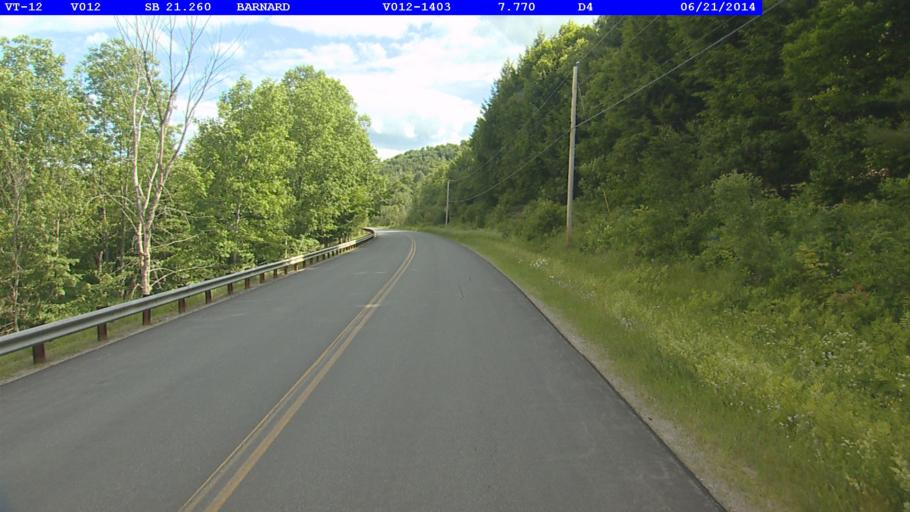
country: US
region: Vermont
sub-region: Orange County
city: Randolph
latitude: 43.7675
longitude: -72.6375
